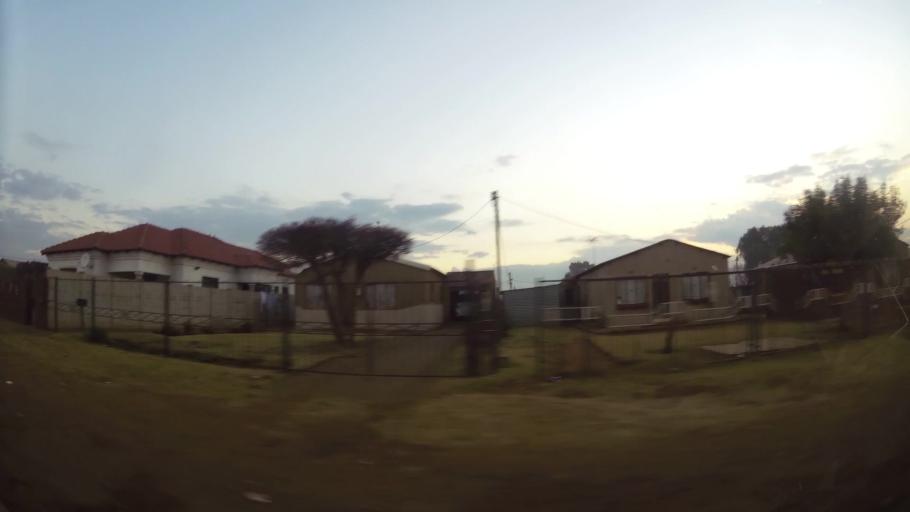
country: ZA
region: Gauteng
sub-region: City of Johannesburg Metropolitan Municipality
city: Orange Farm
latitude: -26.5545
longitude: 27.8606
